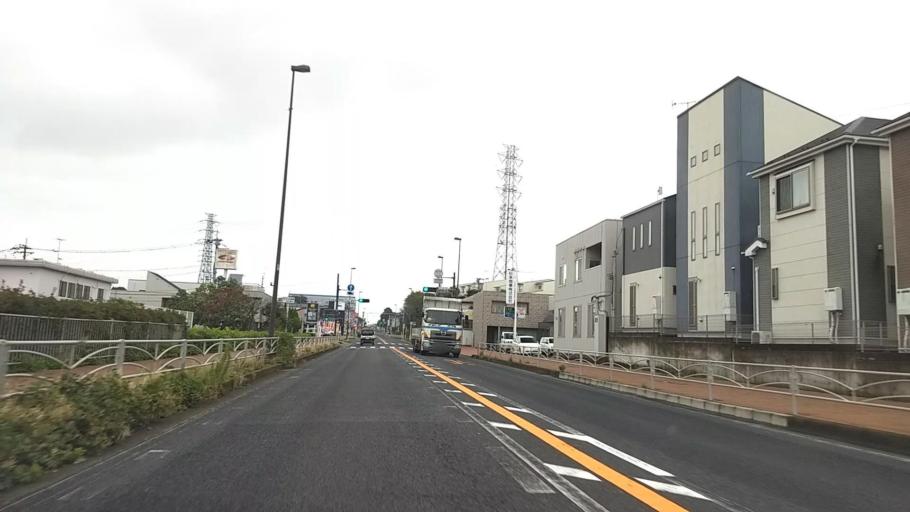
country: JP
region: Kanagawa
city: Isehara
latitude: 35.4110
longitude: 139.3296
